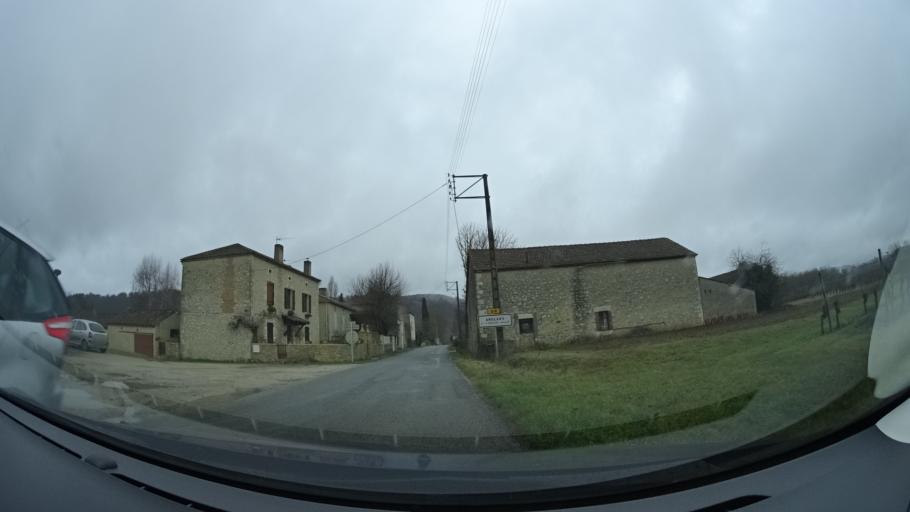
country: FR
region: Midi-Pyrenees
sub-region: Departement du Lot
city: Prayssac
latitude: 44.4923
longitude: 1.2026
